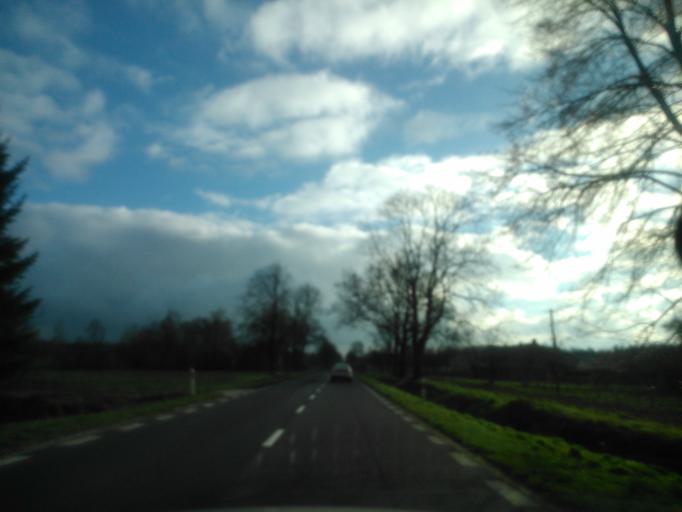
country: PL
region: Masovian Voivodeship
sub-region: Powiat sierpecki
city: Szczutowo
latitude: 52.9135
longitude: 19.6283
